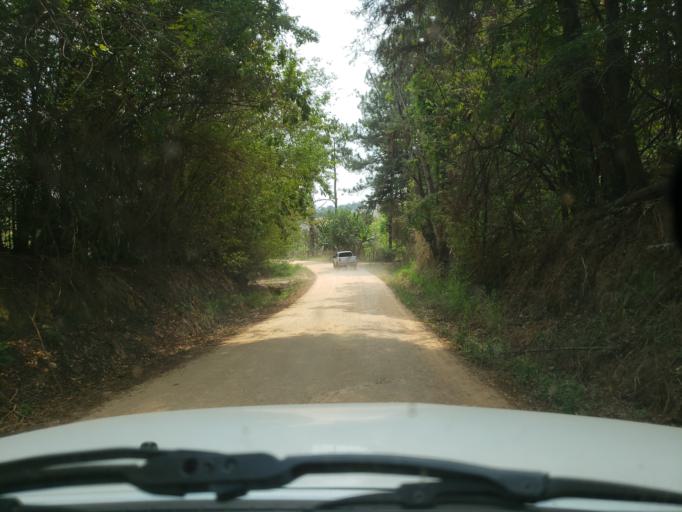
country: BR
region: Minas Gerais
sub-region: Jacutinga
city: Jacutinga
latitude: -22.3147
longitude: -46.6030
